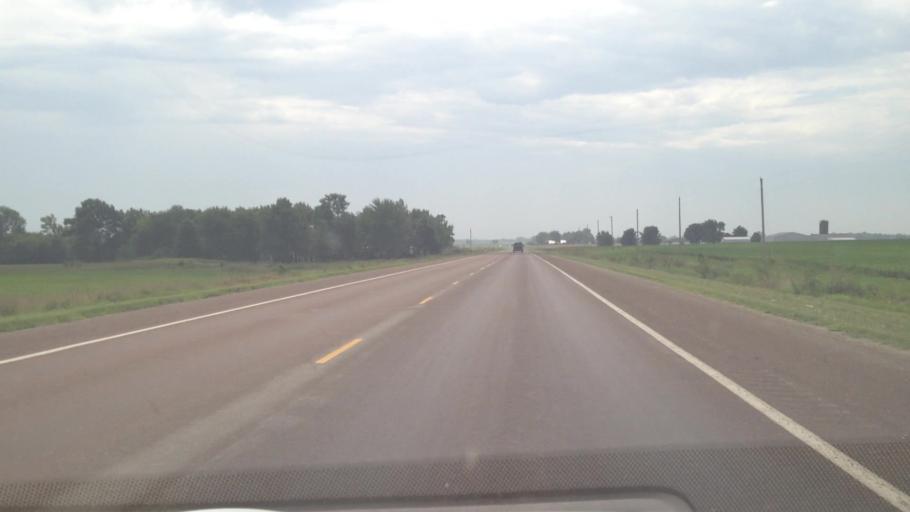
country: US
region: Kansas
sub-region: Crawford County
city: Girard
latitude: 37.4948
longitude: -94.8426
